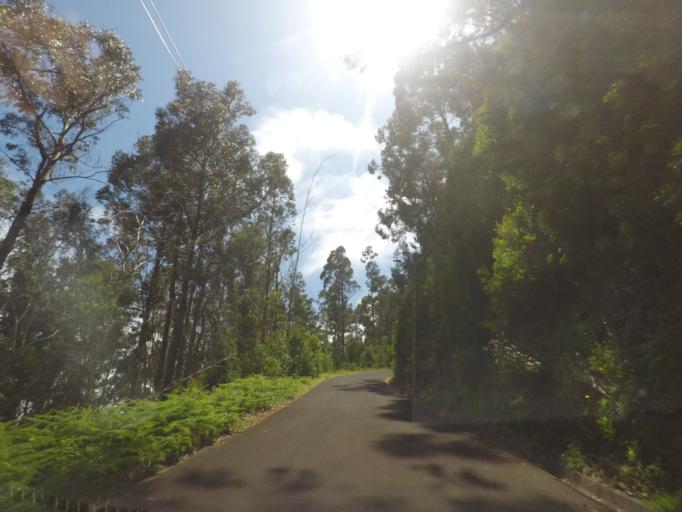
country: PT
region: Madeira
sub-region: Calheta
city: Arco da Calheta
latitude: 32.7278
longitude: -17.1314
